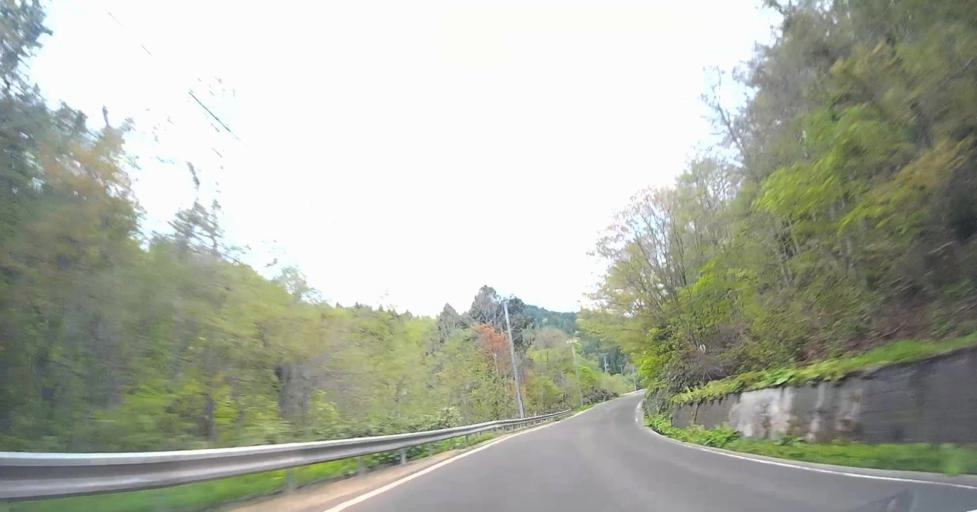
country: JP
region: Aomori
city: Goshogawara
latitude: 41.1018
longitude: 140.5511
